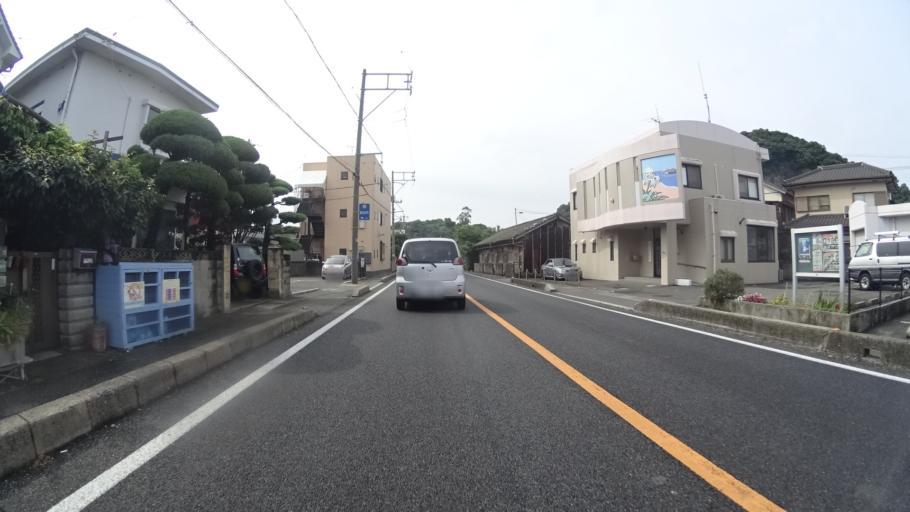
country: JP
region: Yamaguchi
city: Shimonoseki
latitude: 34.0679
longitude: 130.9045
